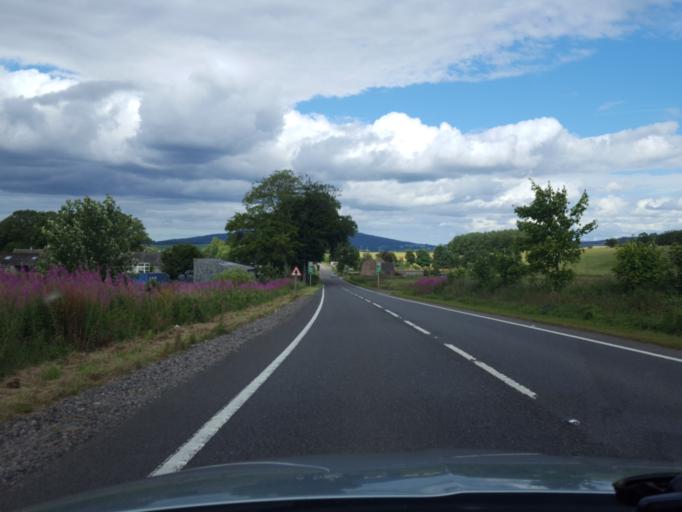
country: GB
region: Scotland
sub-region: Moray
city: Rothes
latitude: 57.4577
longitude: -3.2469
